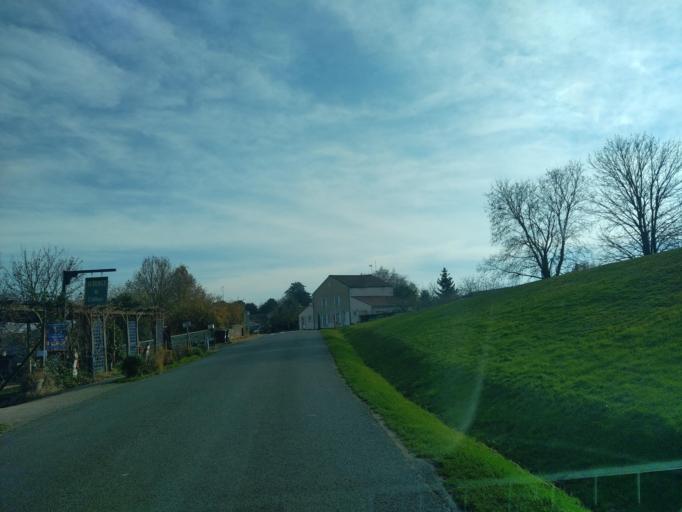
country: FR
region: Pays de la Loire
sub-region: Departement de la Vendee
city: Maillezais
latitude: 46.3733
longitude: -0.7451
